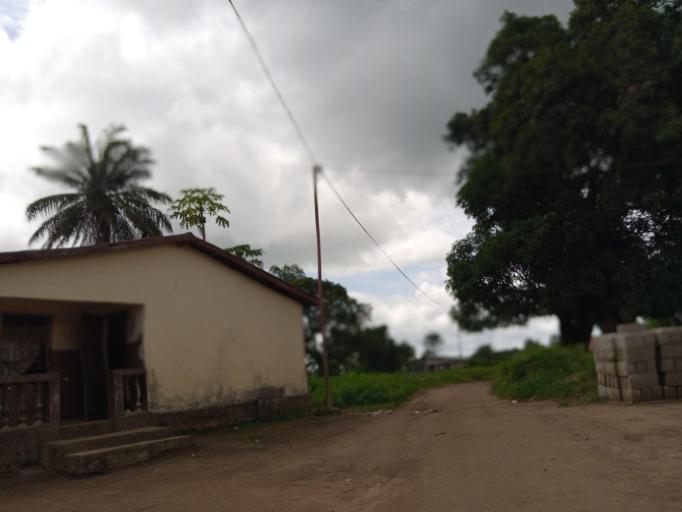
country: SL
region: Northern Province
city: Masoyila
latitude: 8.5856
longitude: -13.1633
